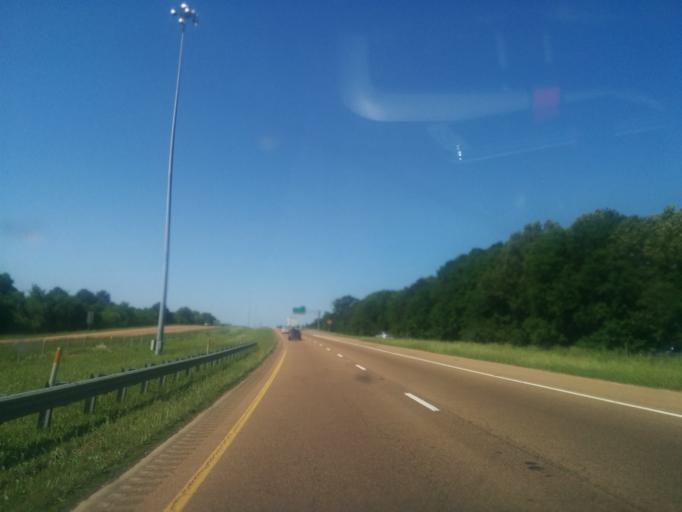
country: US
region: Mississippi
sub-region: Hinds County
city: Jackson
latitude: 32.3308
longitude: -90.2455
